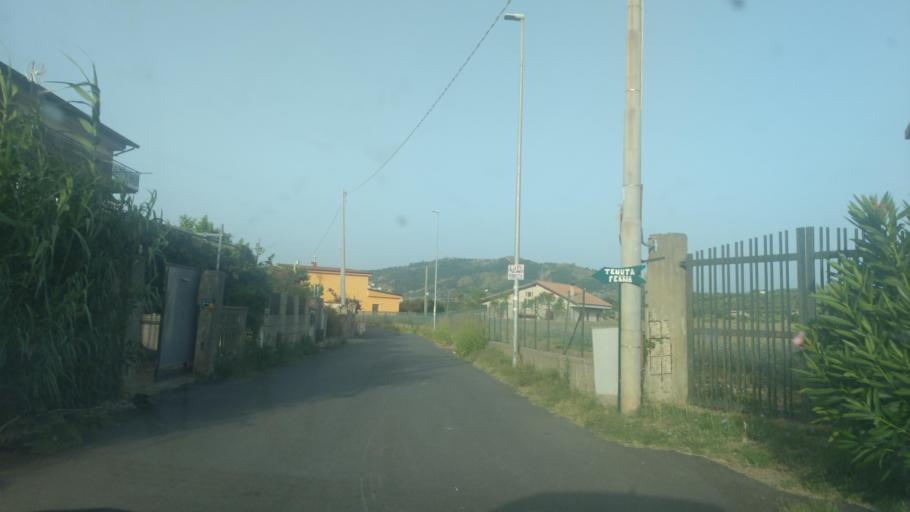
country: IT
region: Calabria
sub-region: Provincia di Catanzaro
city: Staletti
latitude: 38.7655
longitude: 16.5328
